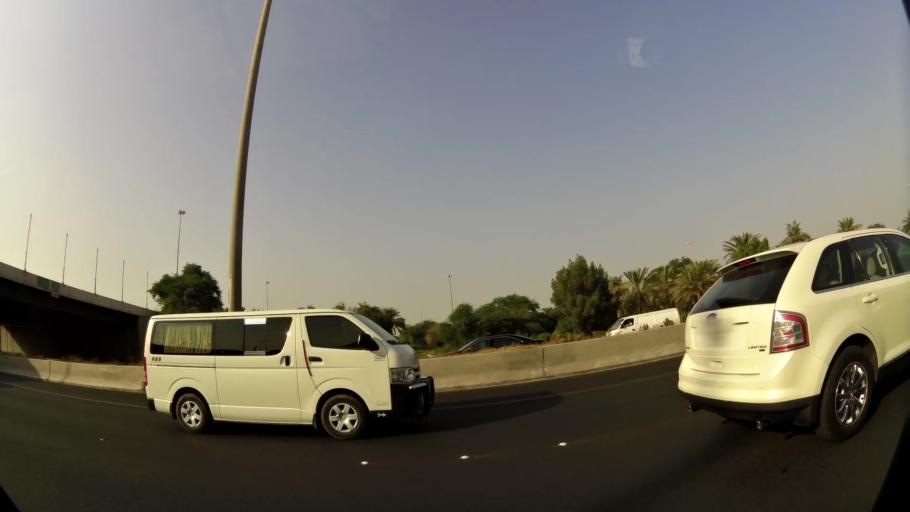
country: KW
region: Al Farwaniyah
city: Al Farwaniyah
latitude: 29.3041
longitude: 47.9797
